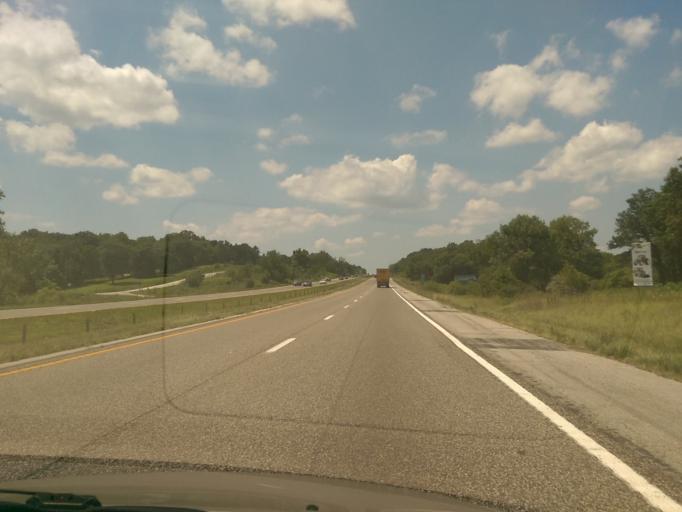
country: US
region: Missouri
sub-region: Boone County
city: Columbia
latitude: 38.9732
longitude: -92.4758
